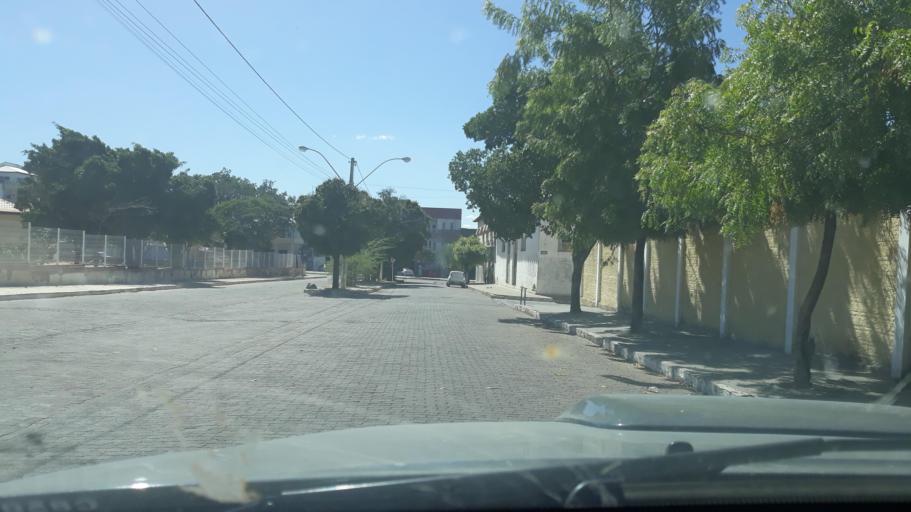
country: BR
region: Bahia
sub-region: Guanambi
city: Guanambi
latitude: -14.2180
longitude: -42.7836
